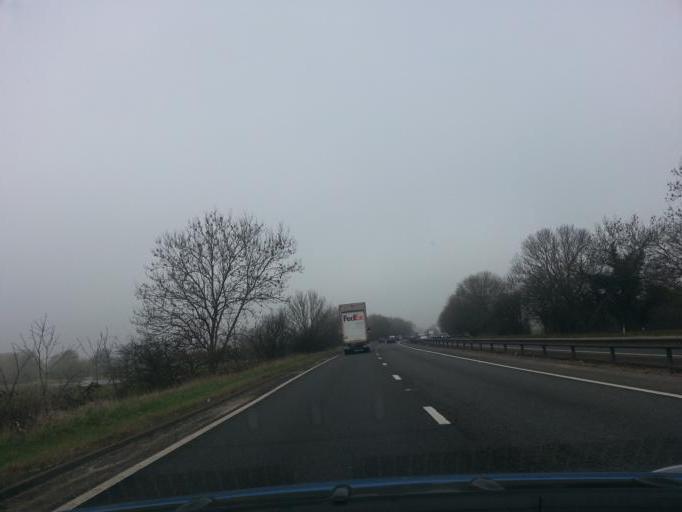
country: GB
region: England
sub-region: Oxfordshire
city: Yarnton
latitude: 51.7713
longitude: -1.3035
